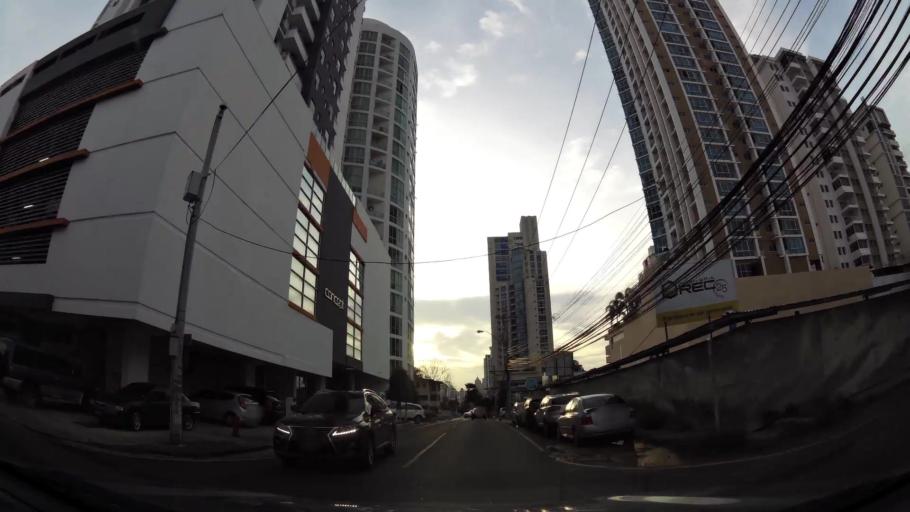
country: PA
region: Panama
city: Panama
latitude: 8.9937
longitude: -79.5110
